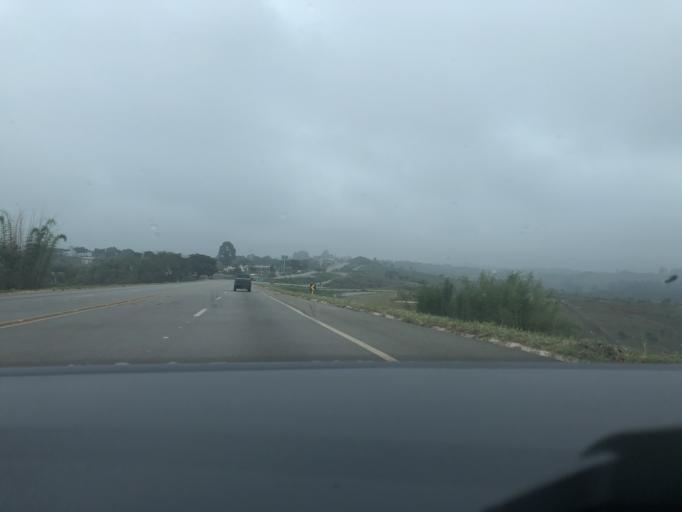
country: BR
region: Minas Gerais
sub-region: Congonhas
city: Congonhas
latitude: -20.6143
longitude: -43.9233
